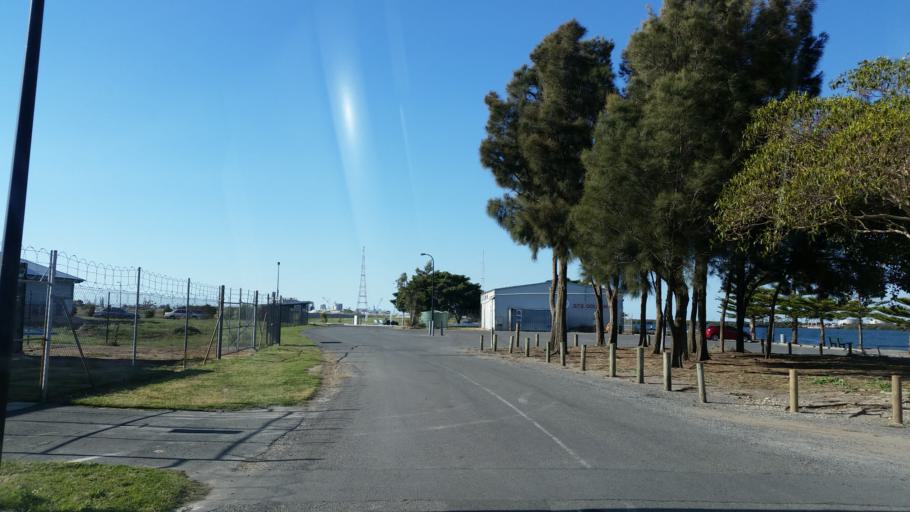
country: AU
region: South Australia
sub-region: Port Adelaide Enfield
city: Birkenhead
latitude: -34.8156
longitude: 138.5114
